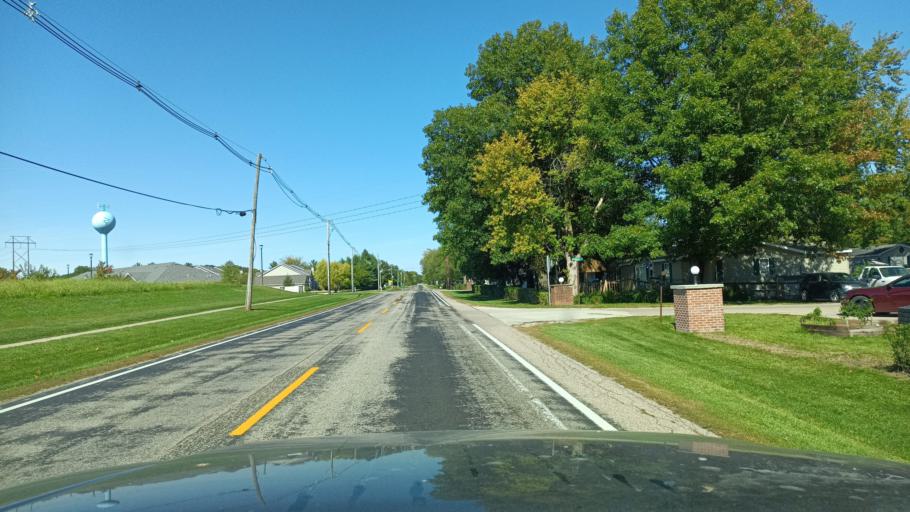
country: US
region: Illinois
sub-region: Champaign County
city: Lake of the Woods
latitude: 40.2015
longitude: -88.3653
